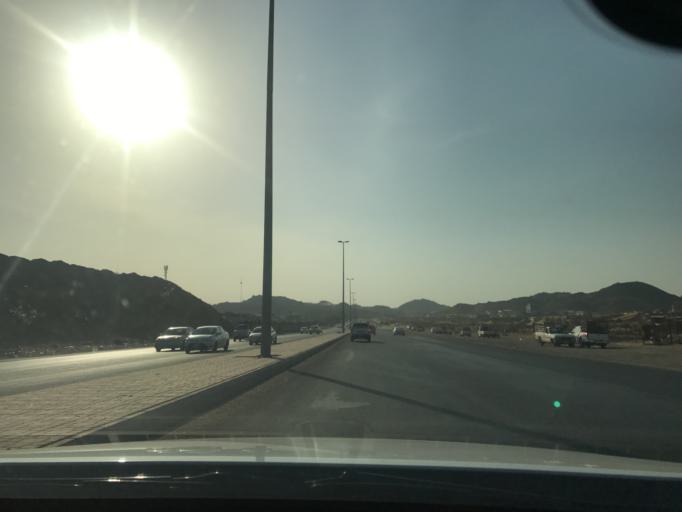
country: SA
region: Makkah
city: Jeddah
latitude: 21.4138
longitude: 39.4175
